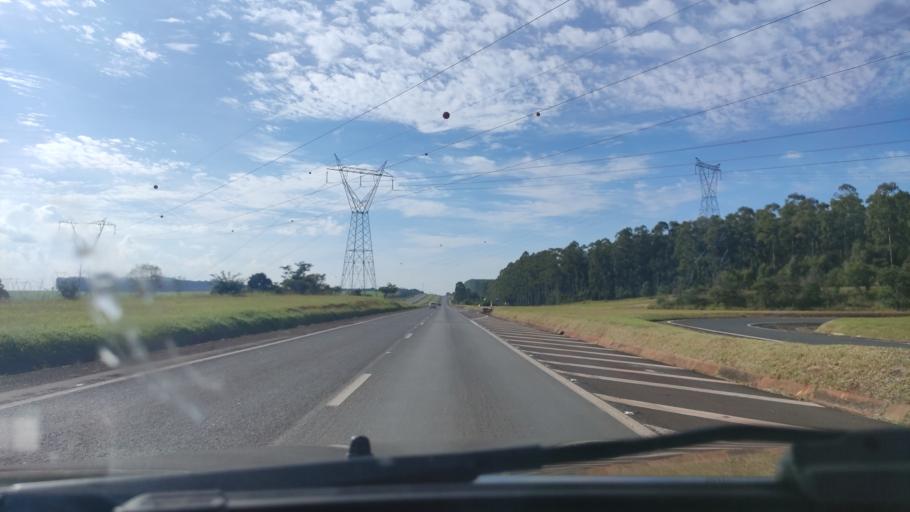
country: BR
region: Sao Paulo
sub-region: Itatinga
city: Itatinga
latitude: -23.0105
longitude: -48.7052
